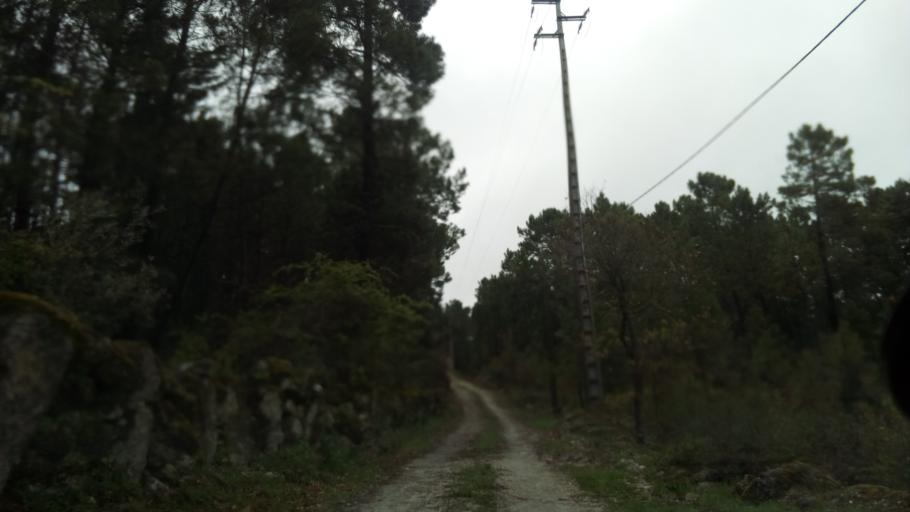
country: PT
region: Guarda
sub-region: Fornos de Algodres
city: Fornos de Algodres
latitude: 40.6234
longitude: -7.5240
